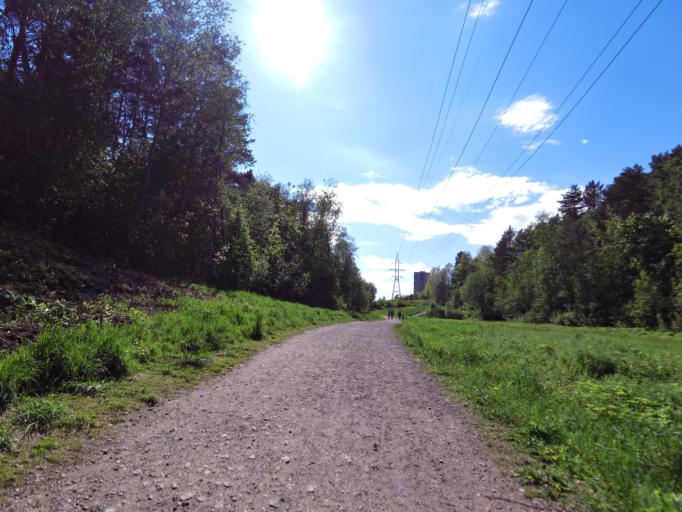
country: LT
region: Vilnius County
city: Seskine
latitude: 54.7207
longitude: 25.2606
